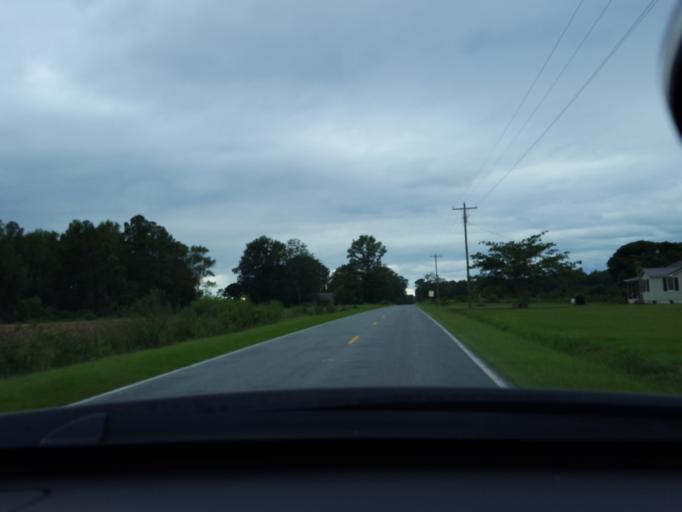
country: US
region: North Carolina
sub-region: Sampson County
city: Clinton
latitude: 34.7776
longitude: -78.3427
